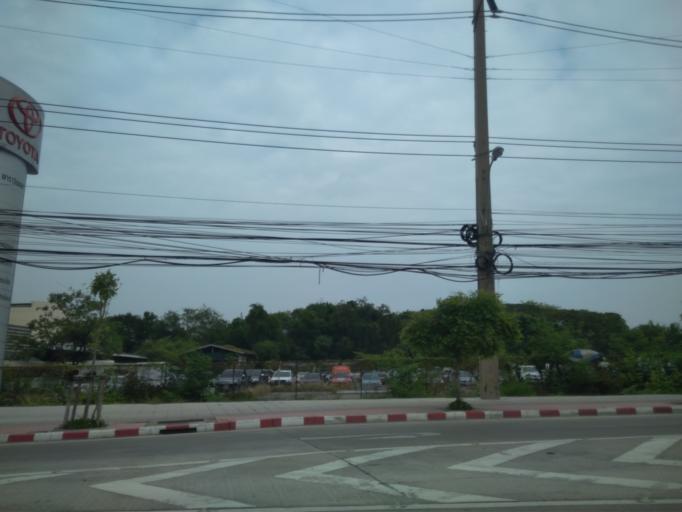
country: TH
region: Bangkok
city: Suan Luang
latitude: 13.7177
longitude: 100.6427
